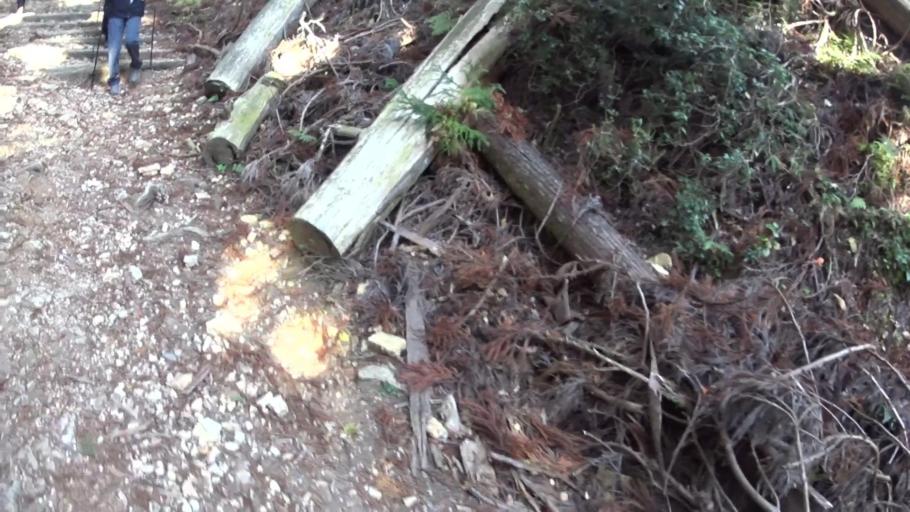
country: JP
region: Kyoto
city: Kameoka
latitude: 35.0496
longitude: 135.6351
